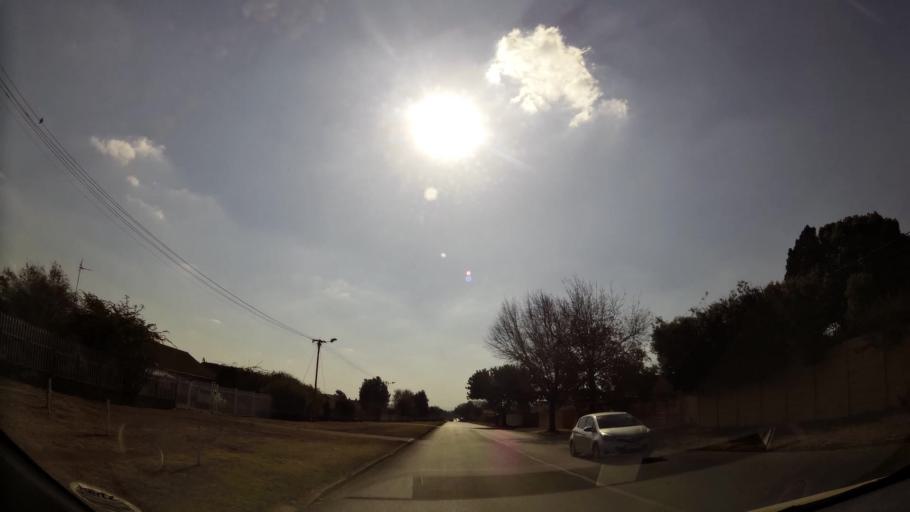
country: ZA
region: Gauteng
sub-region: West Rand District Municipality
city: Randfontein
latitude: -26.1631
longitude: 27.6950
